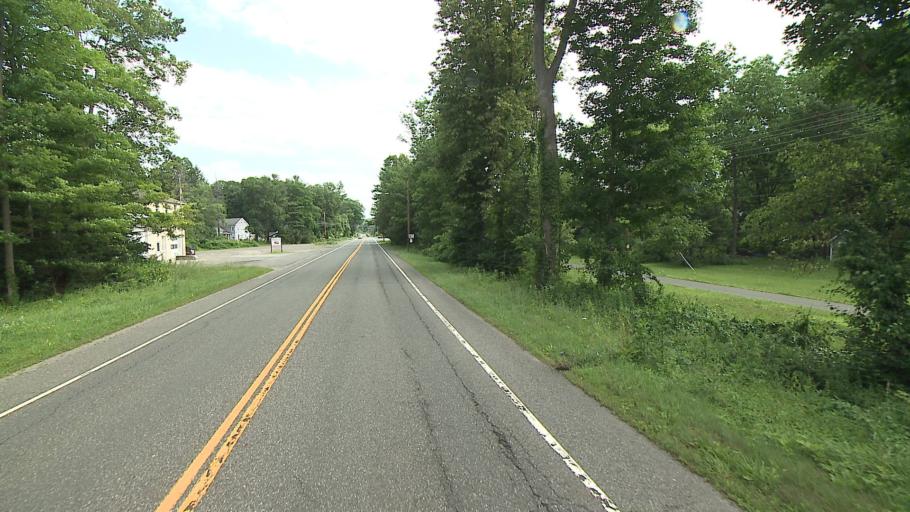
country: US
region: Connecticut
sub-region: Litchfield County
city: Winchester Center
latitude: 41.8653
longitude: -73.0861
